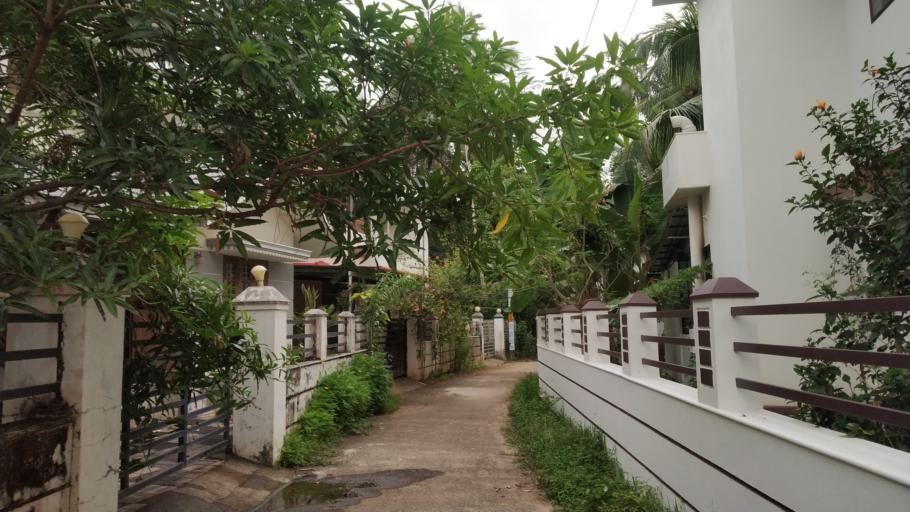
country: IN
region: Kerala
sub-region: Malappuram
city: Tirur
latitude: 10.8858
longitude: 75.9252
